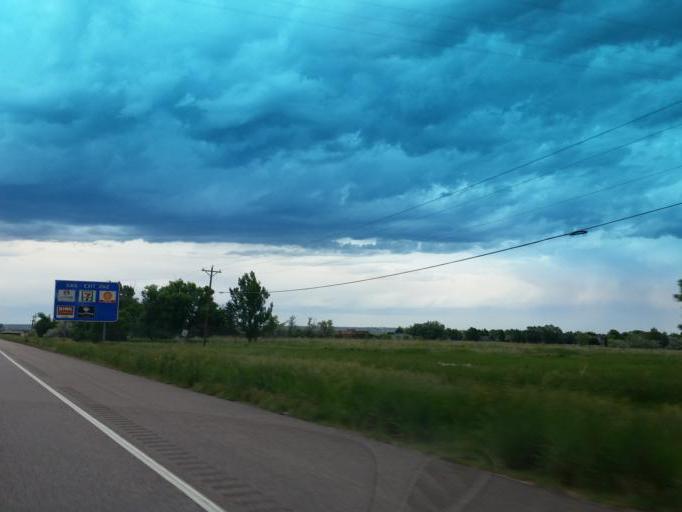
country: US
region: Colorado
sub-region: Weld County
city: Windsor
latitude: 40.4719
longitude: -104.9918
